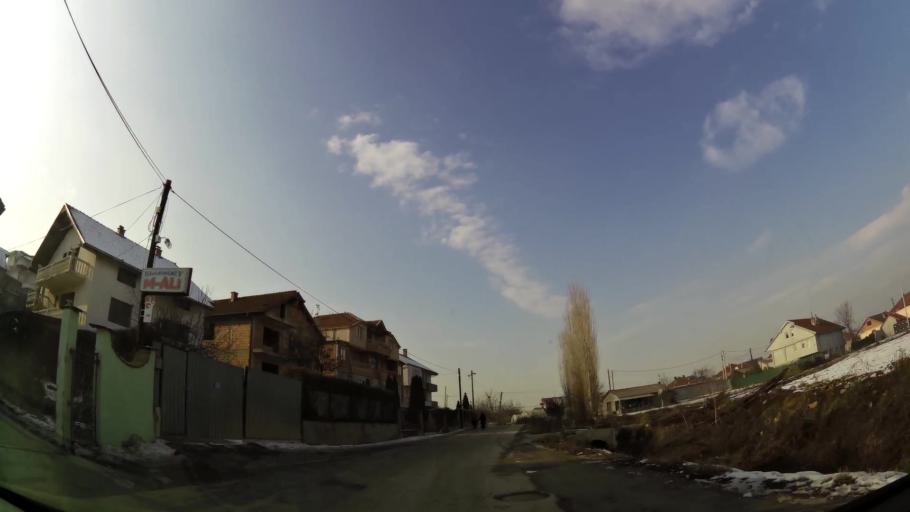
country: MK
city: Creshevo
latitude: 42.0173
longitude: 21.5089
